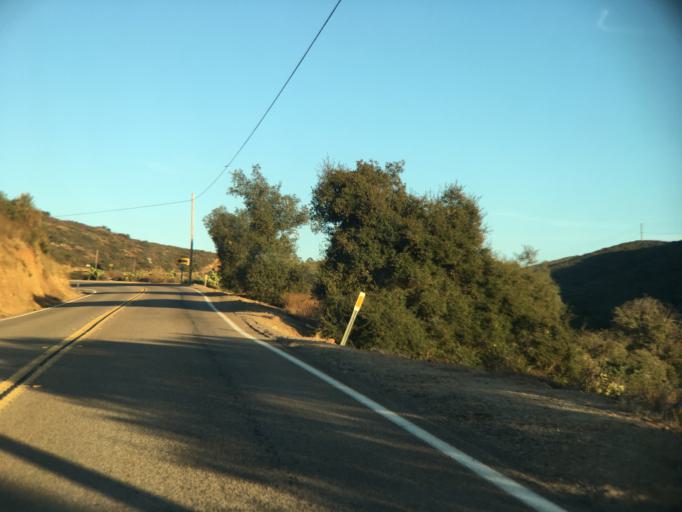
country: US
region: California
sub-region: San Diego County
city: Alpine
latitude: 32.8052
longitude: -116.7887
